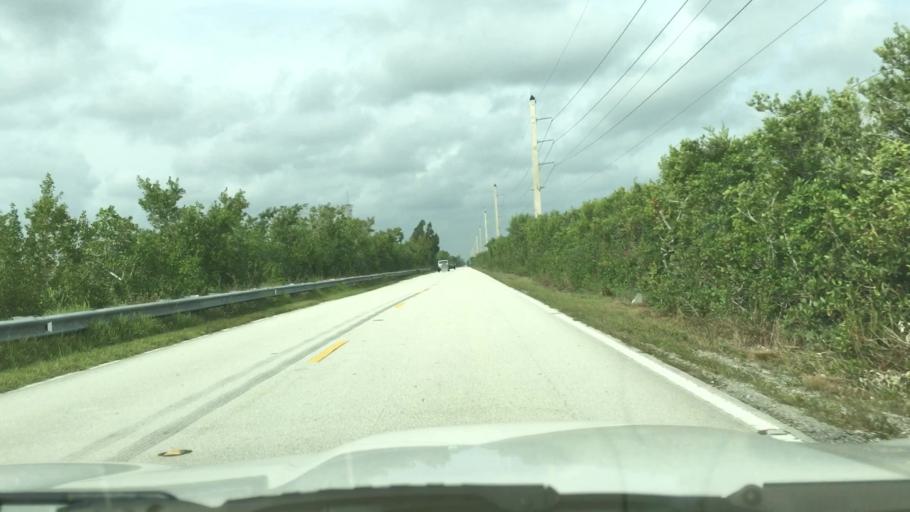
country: US
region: Florida
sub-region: Monroe County
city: North Key Largo
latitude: 25.3198
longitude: -80.3991
